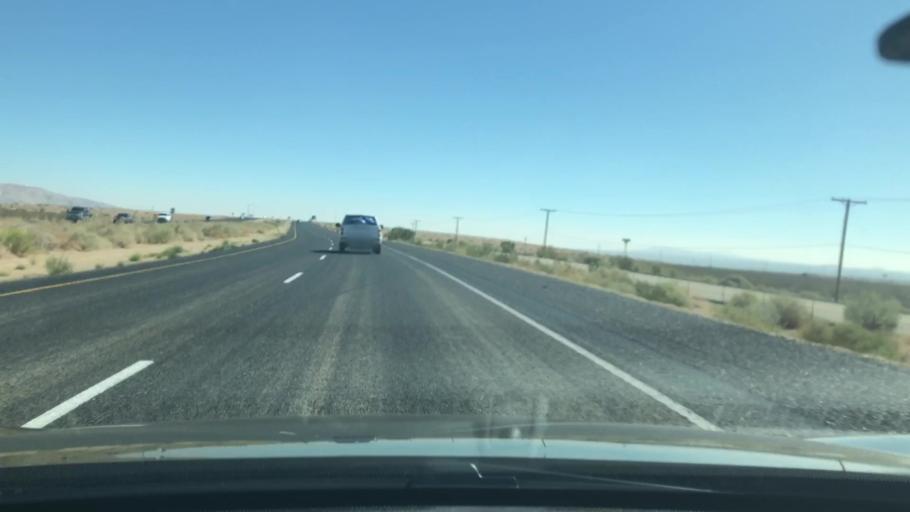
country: US
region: California
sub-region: Kern County
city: Mojave
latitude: 35.0924
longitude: -118.1492
